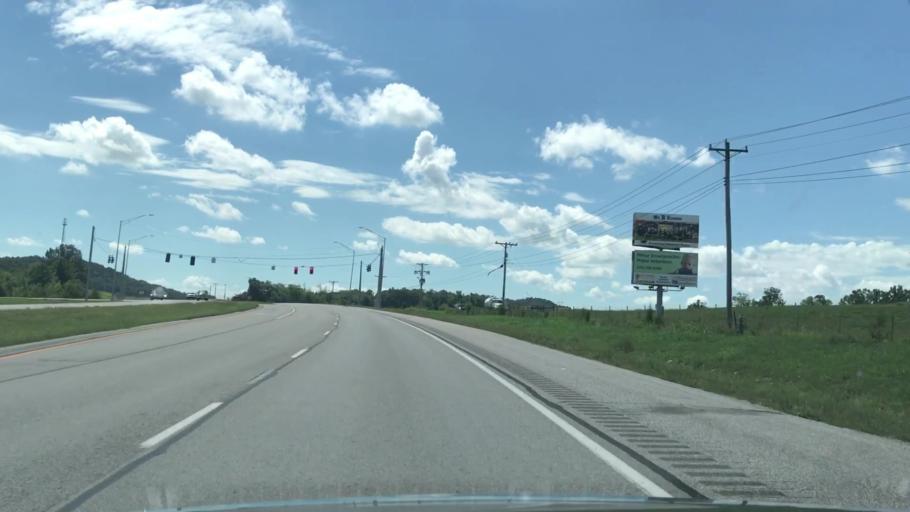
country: US
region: Kentucky
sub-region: Logan County
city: Russellville
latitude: 36.8441
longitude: -86.9201
